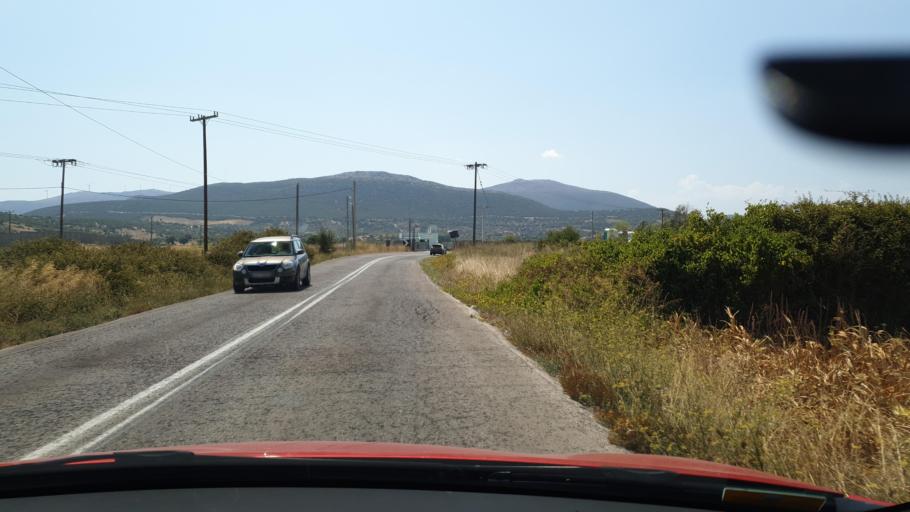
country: GR
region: Central Greece
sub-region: Nomos Evvoias
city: Aliveri
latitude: 38.4010
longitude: 24.1063
